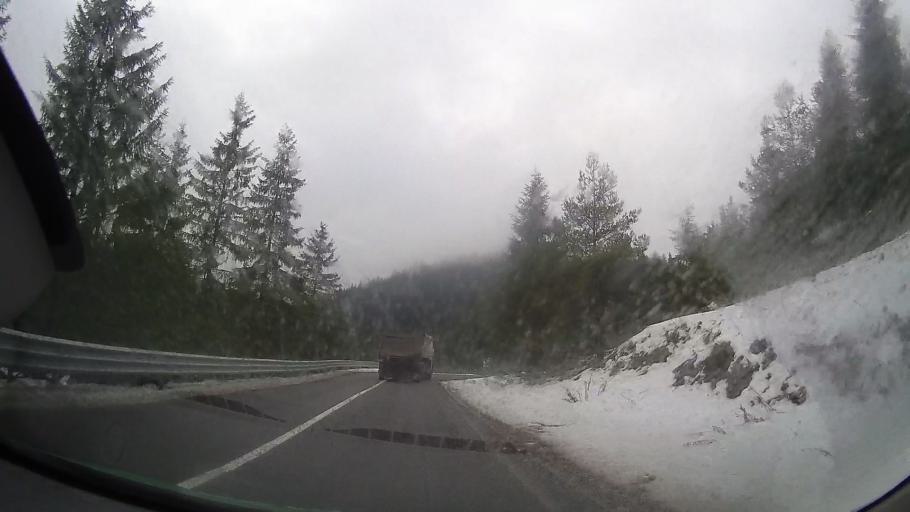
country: RO
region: Neamt
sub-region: Comuna Bicaz Chei
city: Bicaz Chei
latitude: 46.7796
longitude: 25.7523
